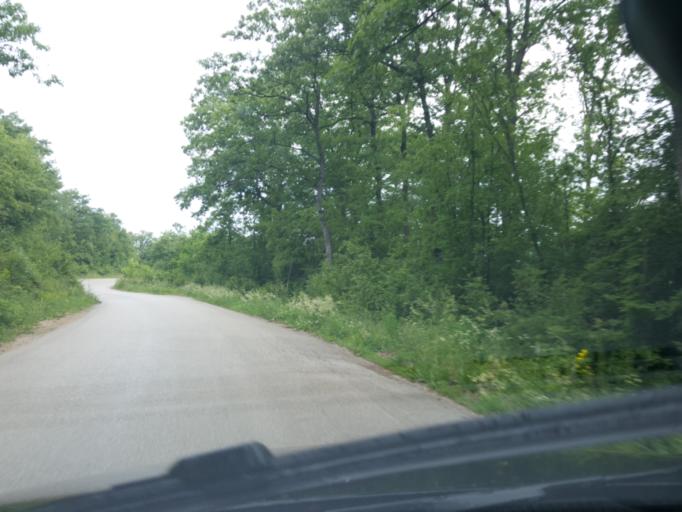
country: RS
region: Central Serbia
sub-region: Zajecarski Okrug
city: Boljevac
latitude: 43.8087
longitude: 21.8937
